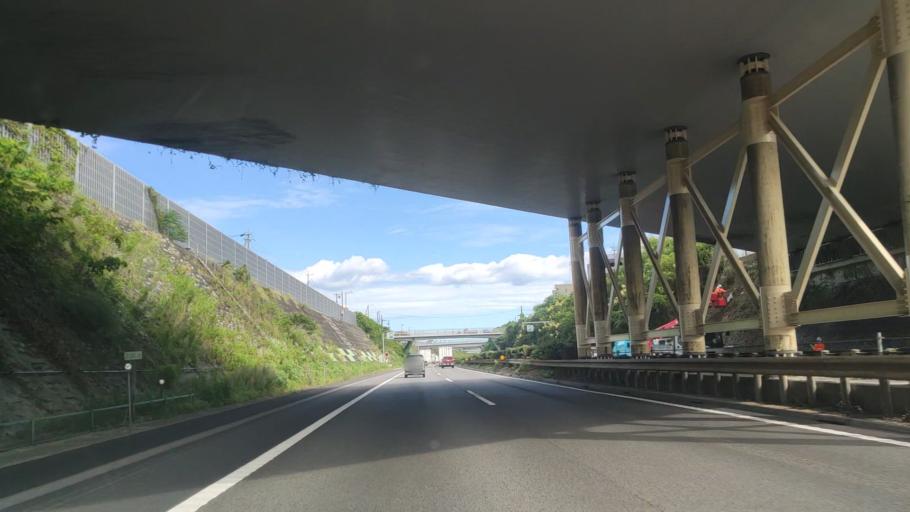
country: JP
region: Shizuoka
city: Hamamatsu
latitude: 34.7652
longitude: 137.7188
